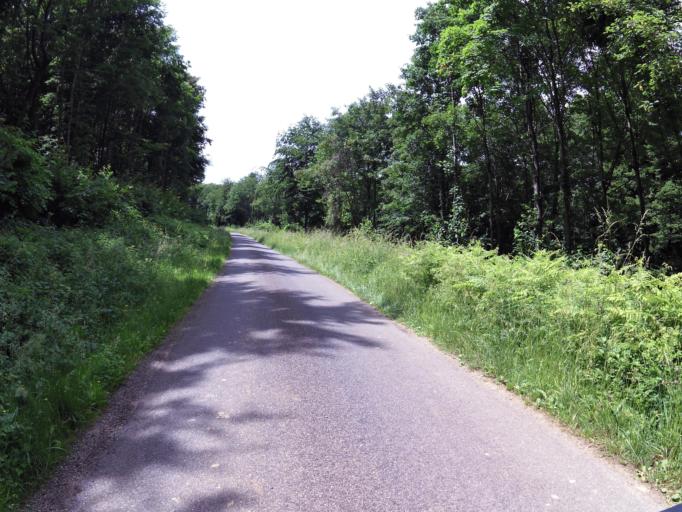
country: FR
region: Lorraine
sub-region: Departement de la Meuse
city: Stenay
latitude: 49.5397
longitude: 5.1411
